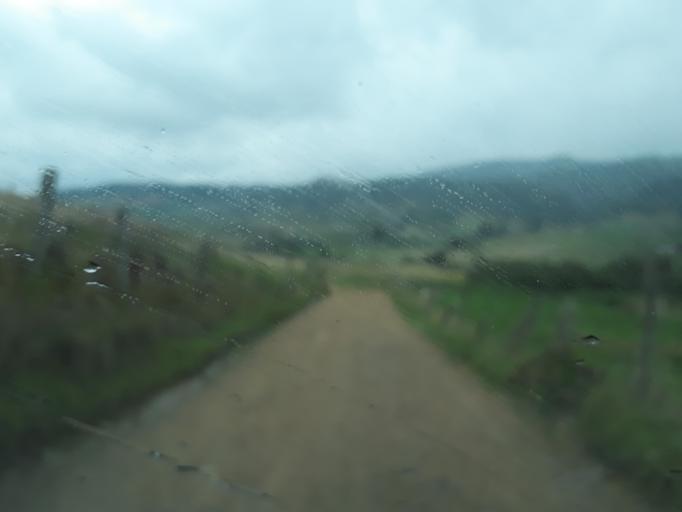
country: CO
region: Cundinamarca
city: Lenguazaque
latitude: 5.2788
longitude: -73.6548
